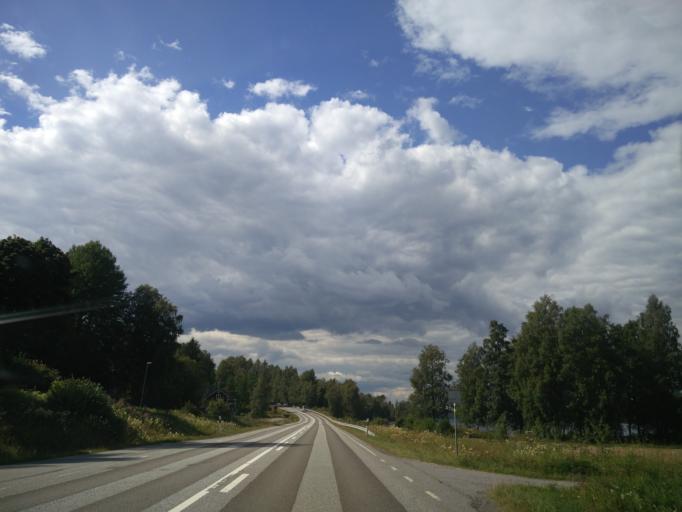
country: SE
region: OErebro
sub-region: Hallefors Kommun
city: Haellefors
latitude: 59.7419
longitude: 14.4651
